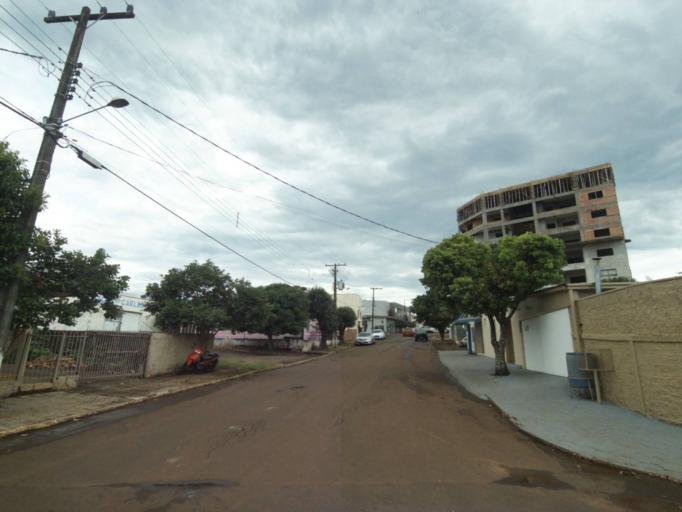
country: BR
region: Parana
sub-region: Guaraniacu
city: Guaraniacu
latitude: -25.0979
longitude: -52.8687
